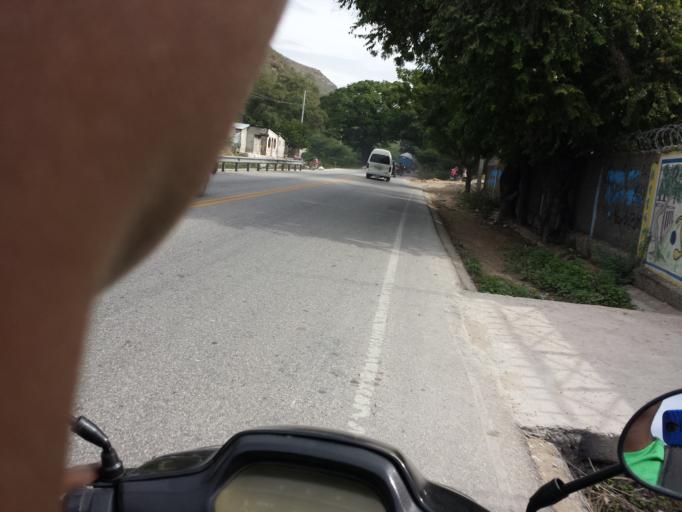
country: HT
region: Artibonite
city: Saint-Marc
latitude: 19.1251
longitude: -72.6947
